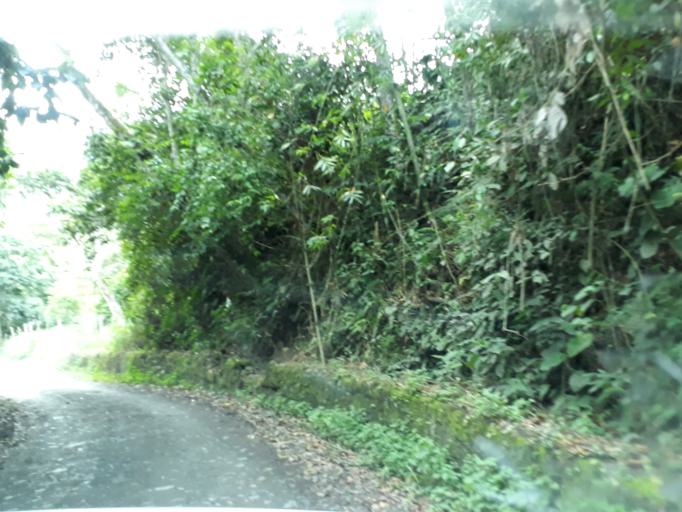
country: CO
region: Cundinamarca
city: Pacho
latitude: 5.1918
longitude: -74.2458
